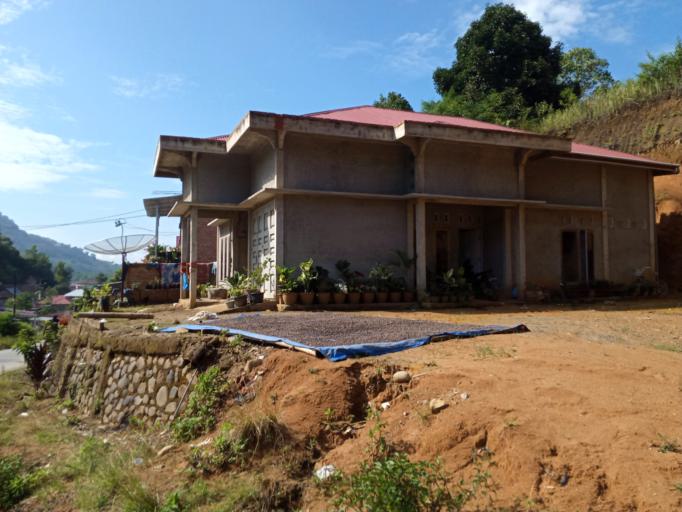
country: ID
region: Jambi
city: Sungai Penuh
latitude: -2.1635
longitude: 101.5906
